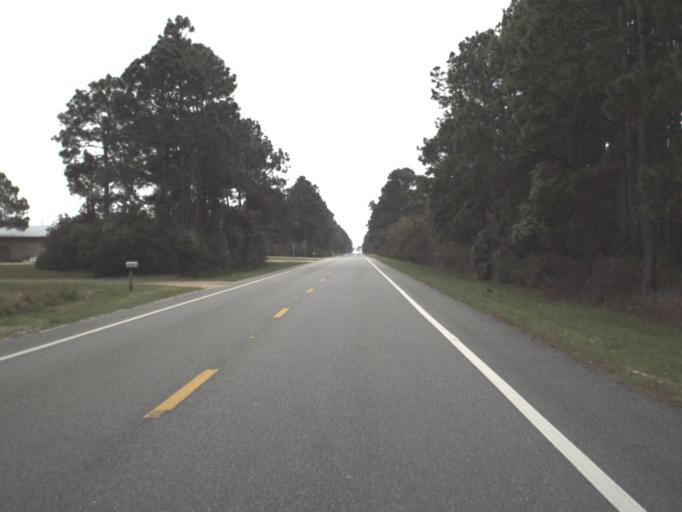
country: US
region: Florida
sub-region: Franklin County
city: Eastpoint
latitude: 29.7754
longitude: -84.8320
